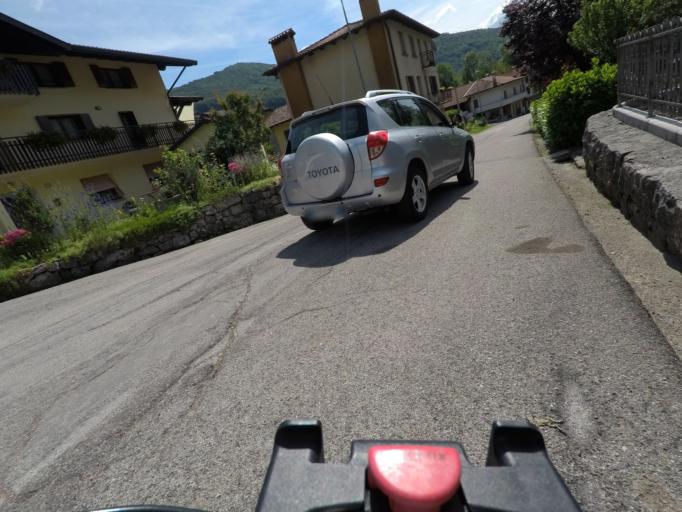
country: IT
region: Friuli Venezia Giulia
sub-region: Provincia di Udine
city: Pulfero
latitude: 46.1587
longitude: 13.4784
